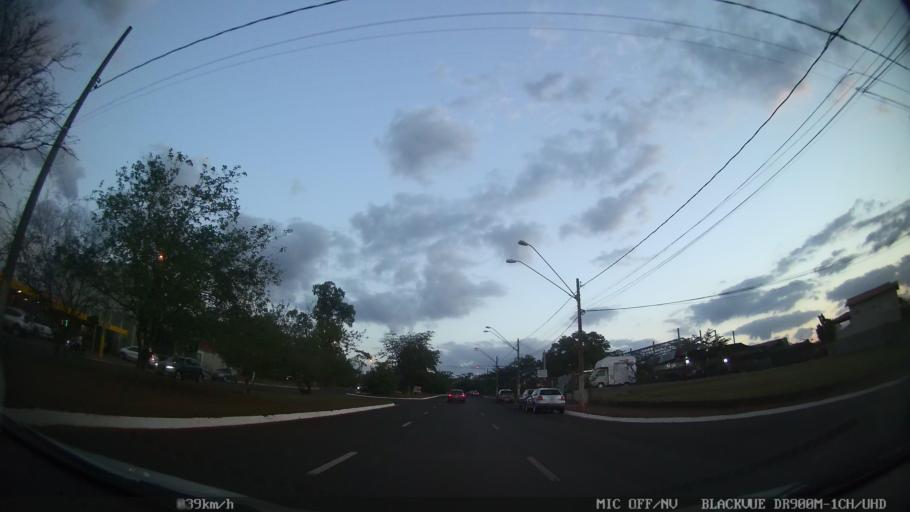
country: BR
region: Sao Paulo
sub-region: Ribeirao Preto
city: Ribeirao Preto
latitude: -21.2141
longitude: -47.7798
